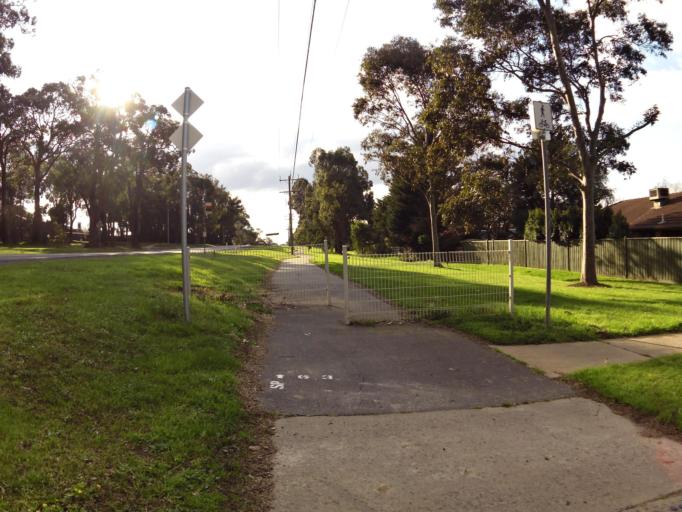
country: AU
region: Victoria
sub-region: Knox
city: The Basin
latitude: -37.8470
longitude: 145.3037
